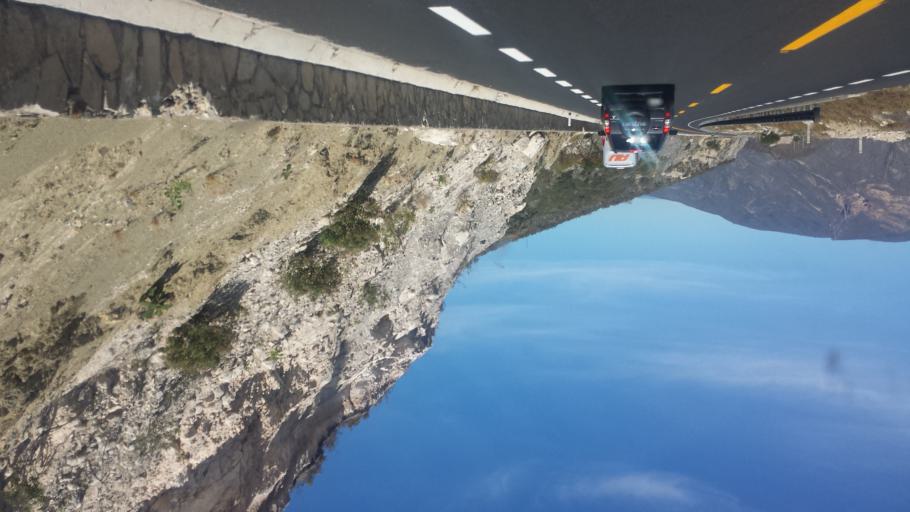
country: MX
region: Puebla
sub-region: San Jose Miahuatlan
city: San Pedro Tetitlan
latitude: 18.0792
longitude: -97.3516
